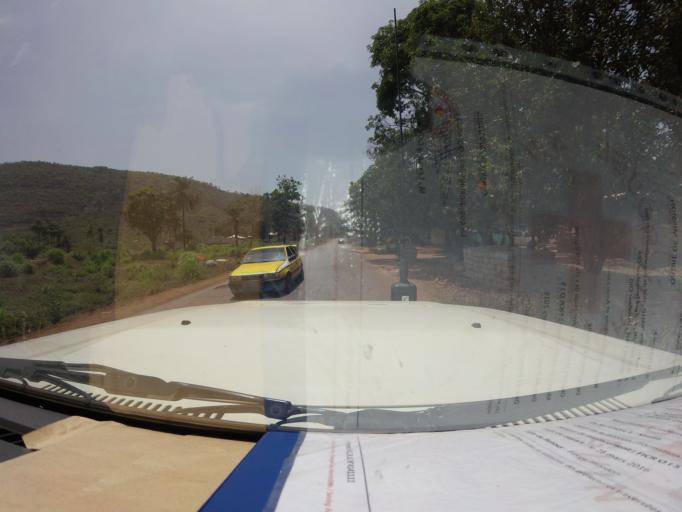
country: GN
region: Kindia
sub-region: Coyah
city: Coyah
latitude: 9.7839
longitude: -13.3212
